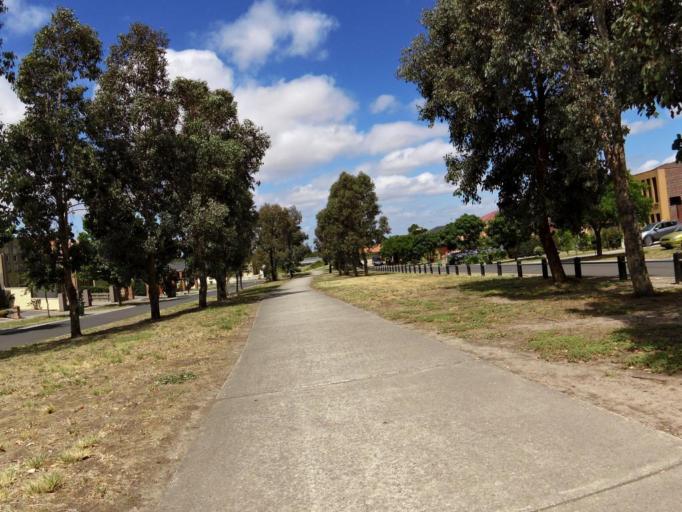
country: AU
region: Victoria
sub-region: Hume
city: Roxburgh Park
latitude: -37.6154
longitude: 144.9248
